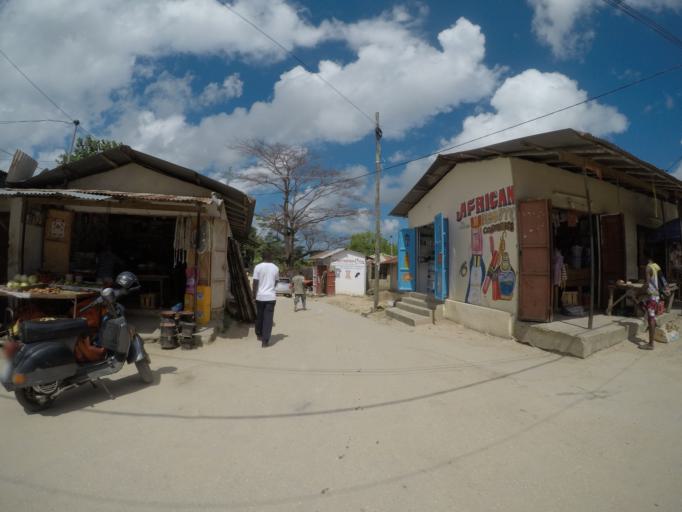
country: TZ
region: Pemba South
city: Chake Chake
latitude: -5.2364
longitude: 39.7790
